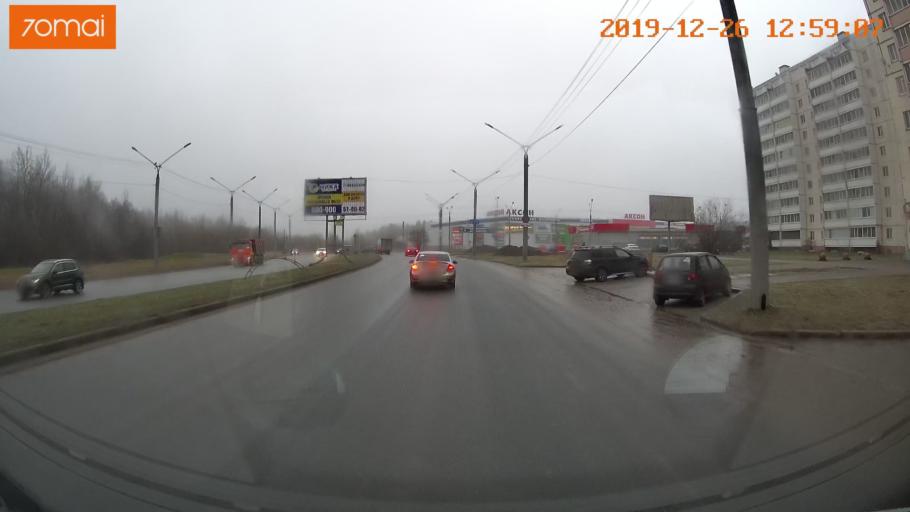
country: RU
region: Vologda
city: Cherepovets
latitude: 59.0811
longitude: 37.9227
